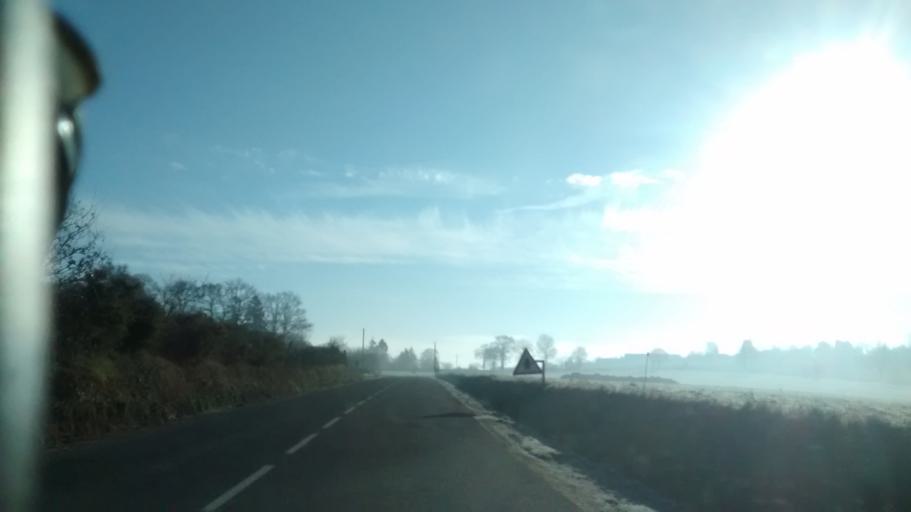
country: FR
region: Brittany
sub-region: Departement d'Ille-et-Vilaine
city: La Bouexiere
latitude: 48.1913
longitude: -1.4504
